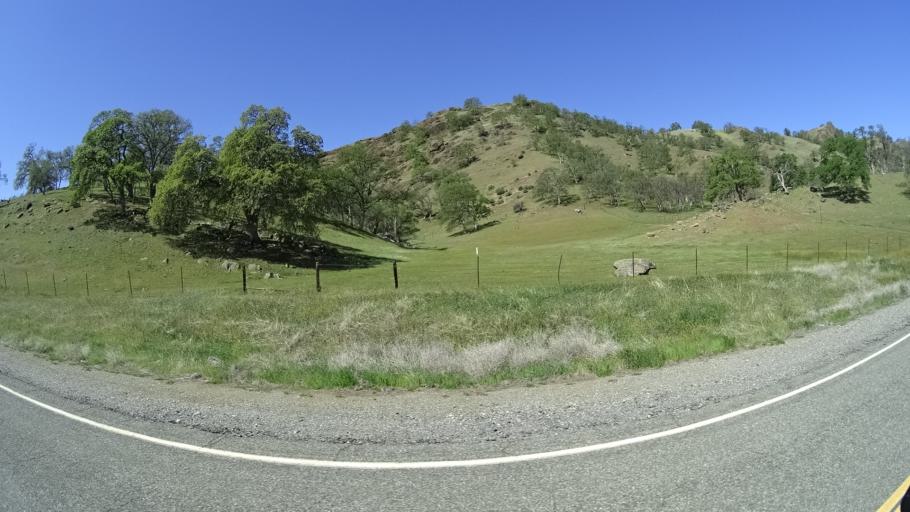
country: US
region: California
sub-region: Tehama County
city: Rancho Tehama Reserve
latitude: 39.7684
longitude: -122.5226
